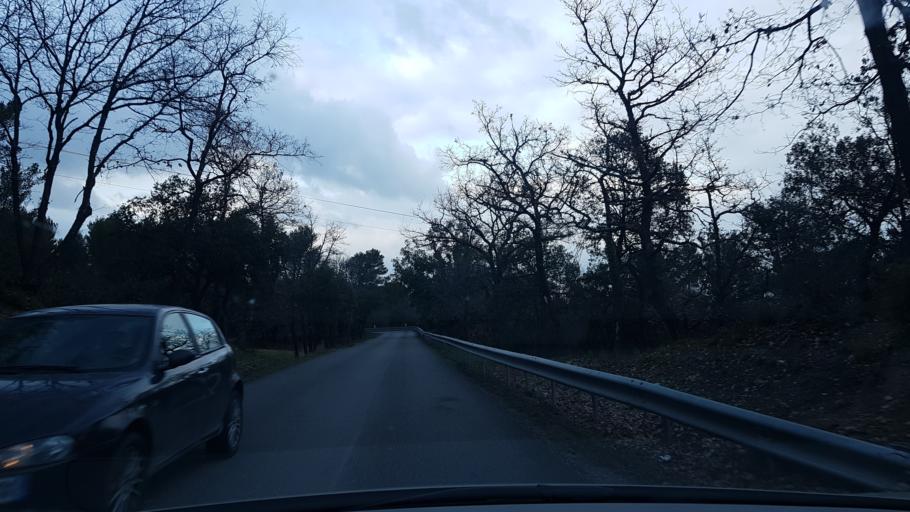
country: FR
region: Provence-Alpes-Cote d'Azur
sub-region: Departement des Bouches-du-Rhone
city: Mimet
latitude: 43.4288
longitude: 5.5094
